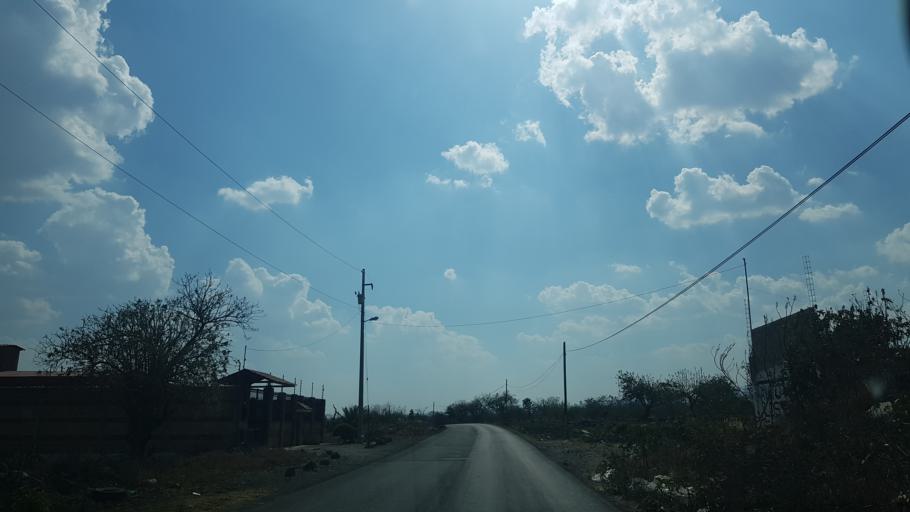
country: MX
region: Puebla
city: Atlixco
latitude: 18.9076
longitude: -98.4777
